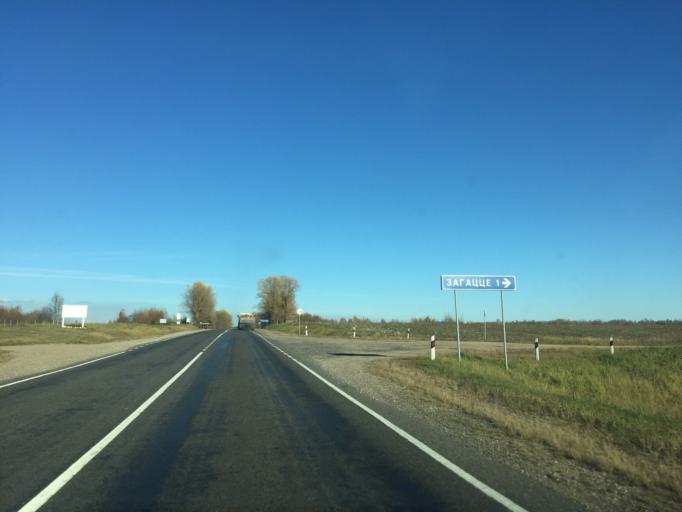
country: BY
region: Vitebsk
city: Dzisna
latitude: 55.3548
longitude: 28.3342
